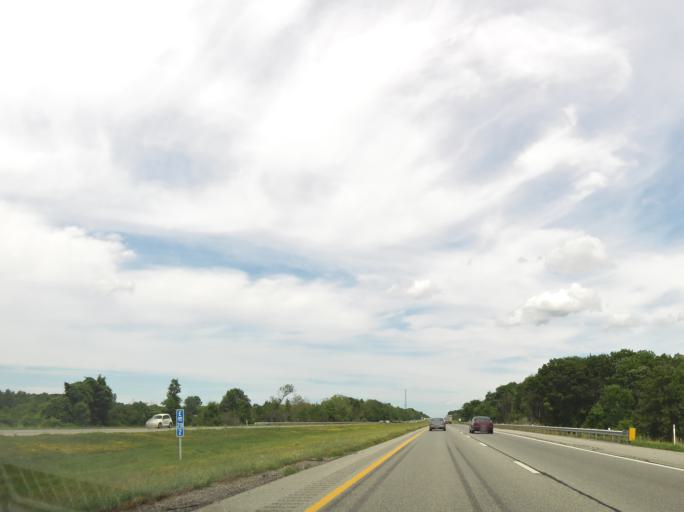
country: US
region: Ohio
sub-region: Lake County
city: Perry
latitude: 41.7401
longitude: -81.0950
